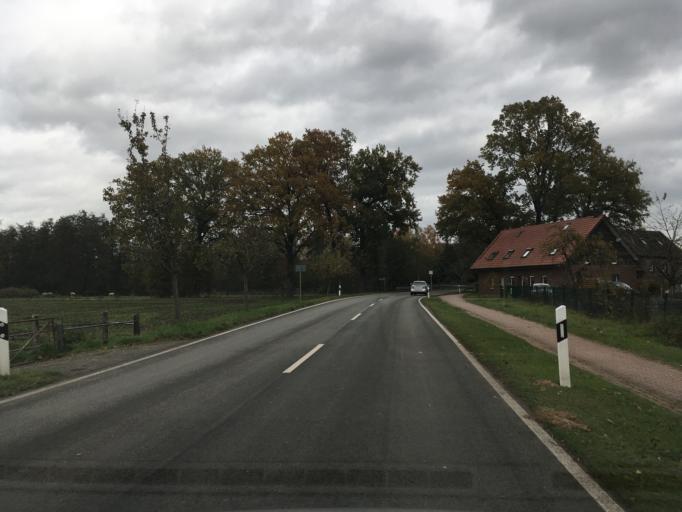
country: DE
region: North Rhine-Westphalia
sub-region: Regierungsbezirk Munster
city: Klein Reken
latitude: 51.8456
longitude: 7.0987
